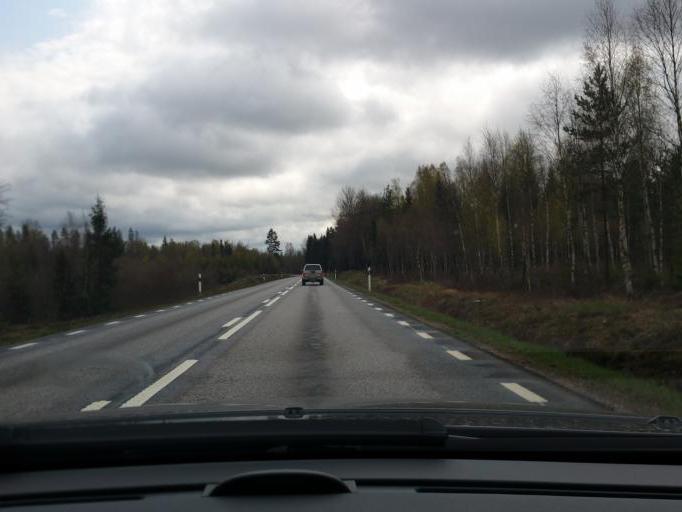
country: SE
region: Kronoberg
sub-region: Vaxjo Kommun
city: Ingelstad
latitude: 56.7877
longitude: 14.8980
